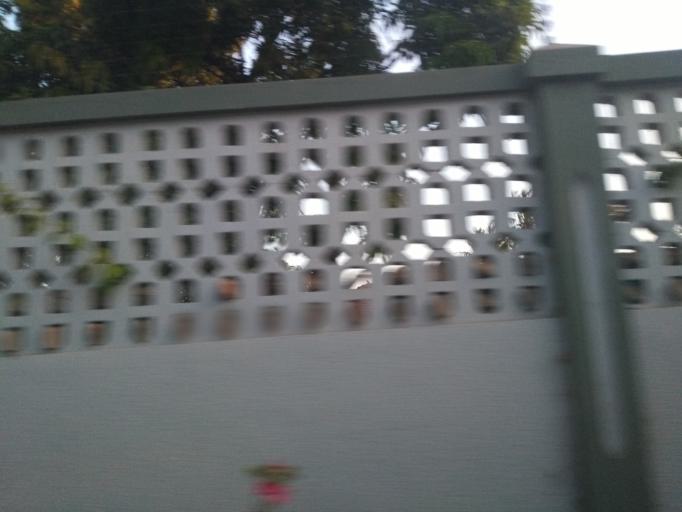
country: TZ
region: Dar es Salaam
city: Magomeni
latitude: -6.7666
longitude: 39.2783
